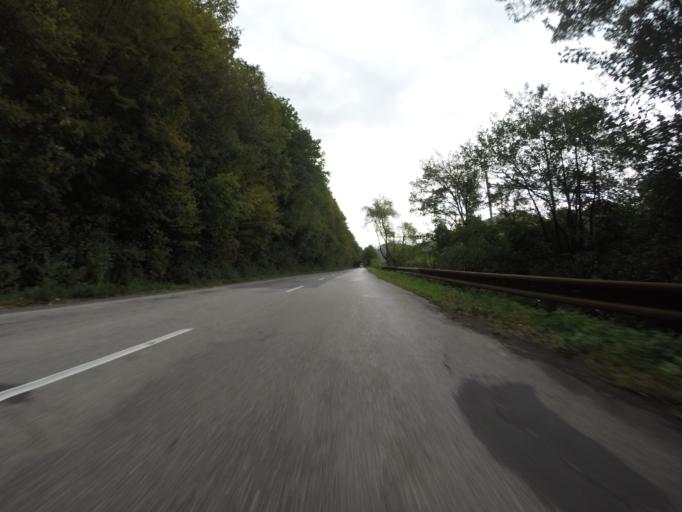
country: SK
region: Banskobystricky
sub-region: Okres Banska Bystrica
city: Zvolen
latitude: 48.5709
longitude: 19.0013
